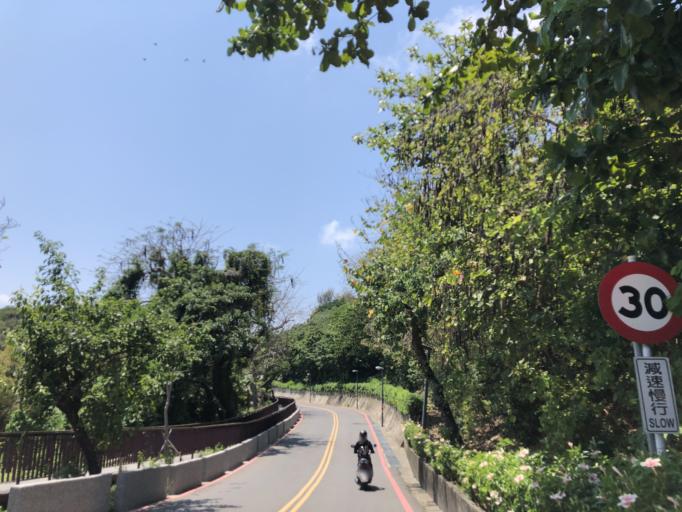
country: TW
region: Kaohsiung
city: Kaohsiung
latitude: 22.6269
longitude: 120.2708
